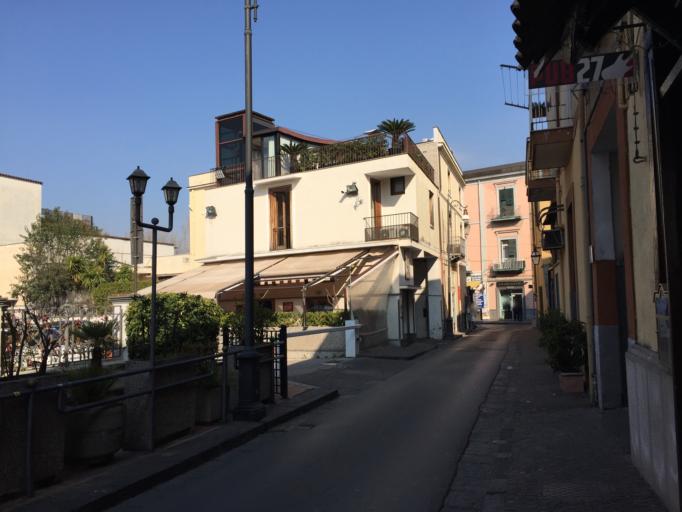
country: IT
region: Campania
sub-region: Provincia di Napoli
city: Pompei
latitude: 40.7490
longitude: 14.4978
